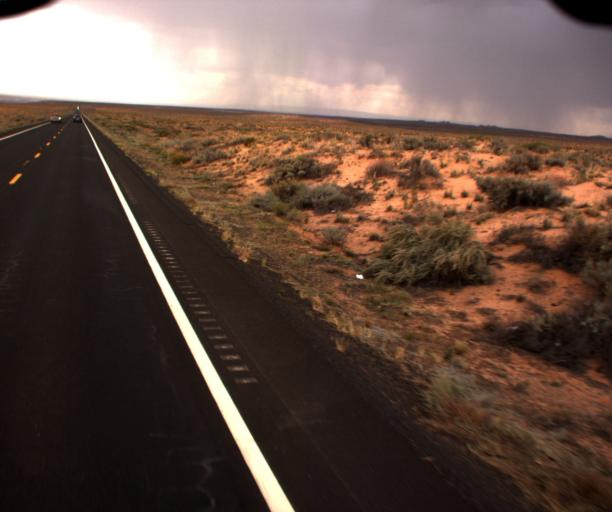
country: US
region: Arizona
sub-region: Coconino County
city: Tuba City
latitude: 36.2083
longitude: -111.0518
